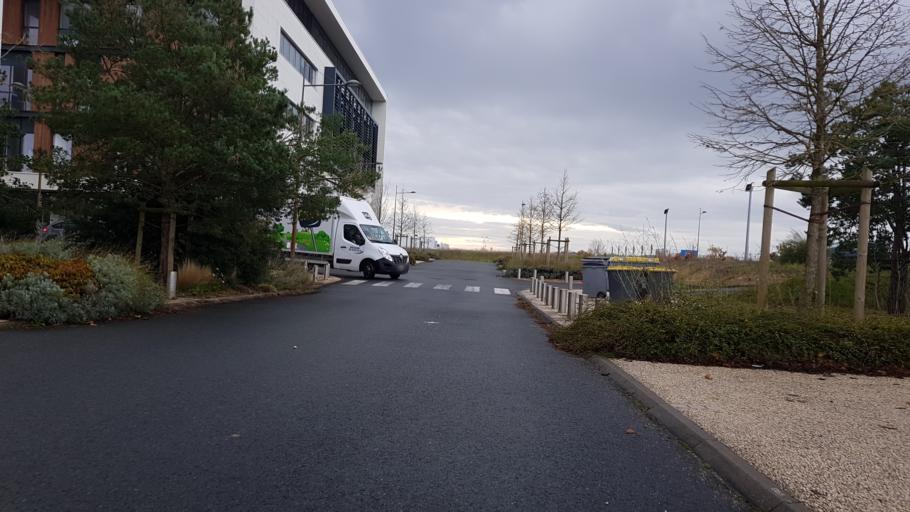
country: FR
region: Poitou-Charentes
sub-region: Departement de la Vienne
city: Chasseneuil-du-Poitou
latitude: 46.6549
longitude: 0.3595
